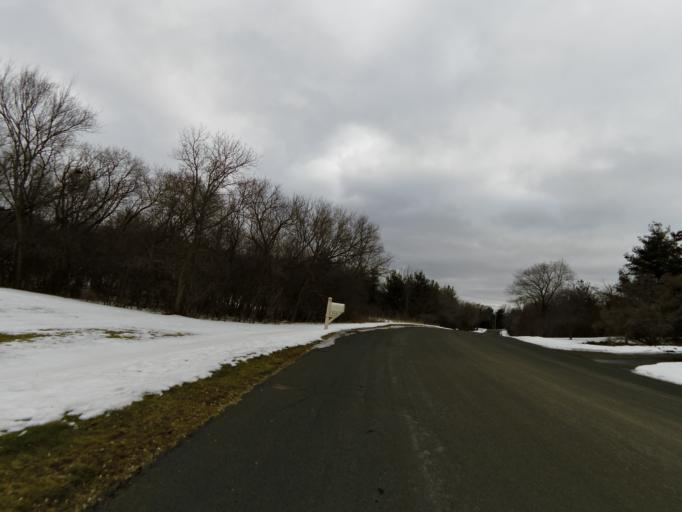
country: US
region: Minnesota
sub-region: Washington County
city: Lake Elmo
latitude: 44.9597
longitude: -92.8361
